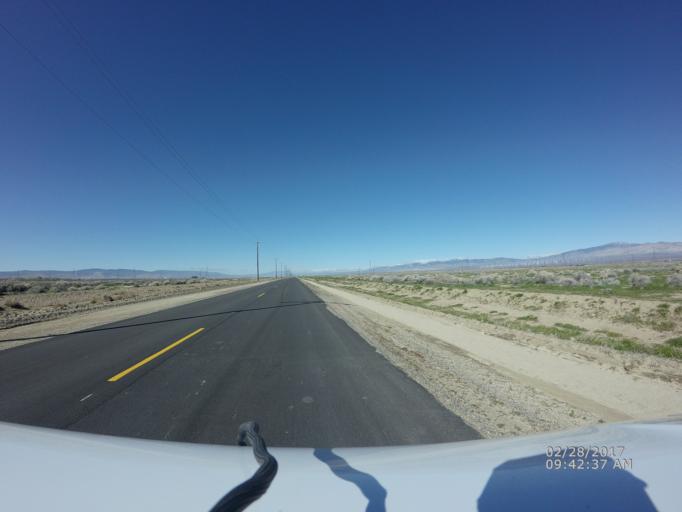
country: US
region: California
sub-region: Kern County
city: Rosamond
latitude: 34.8197
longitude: -118.3295
